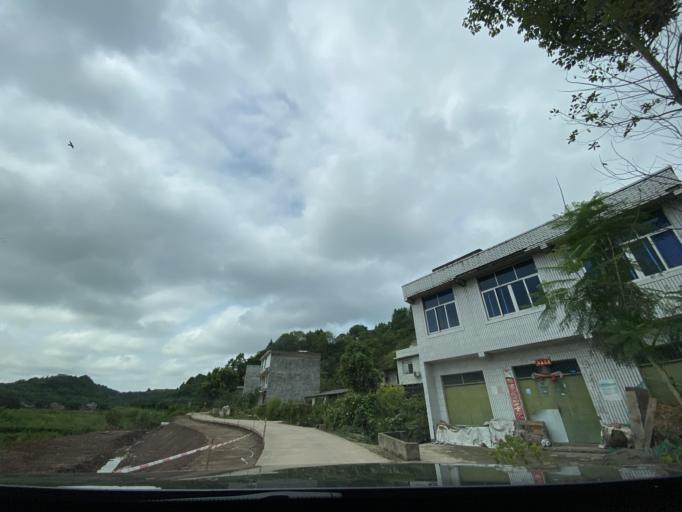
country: CN
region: Sichuan
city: Jiancheng
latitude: 30.4053
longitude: 104.5746
